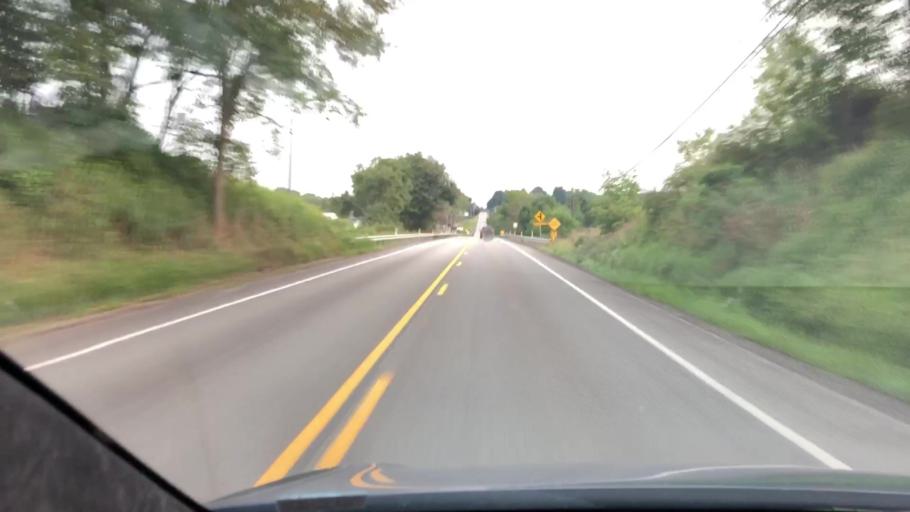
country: US
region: Pennsylvania
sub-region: Butler County
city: Slippery Rock
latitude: 41.1228
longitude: -80.0082
